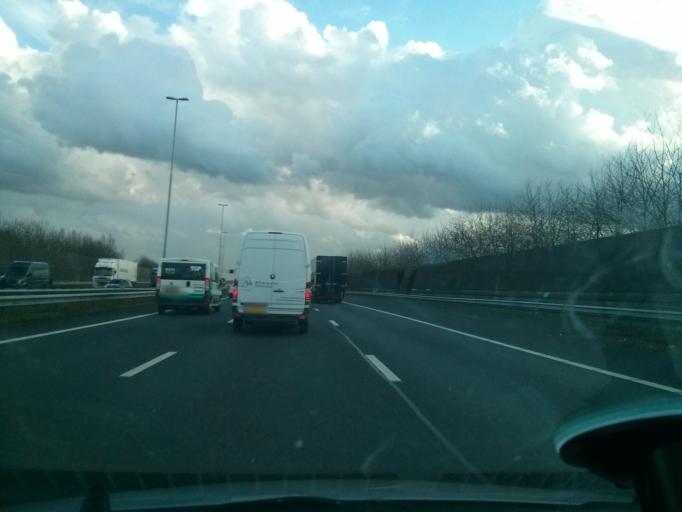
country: NL
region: Gelderland
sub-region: Gemeente Zaltbommel
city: Zaltbommel
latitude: 51.8094
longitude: 5.2592
